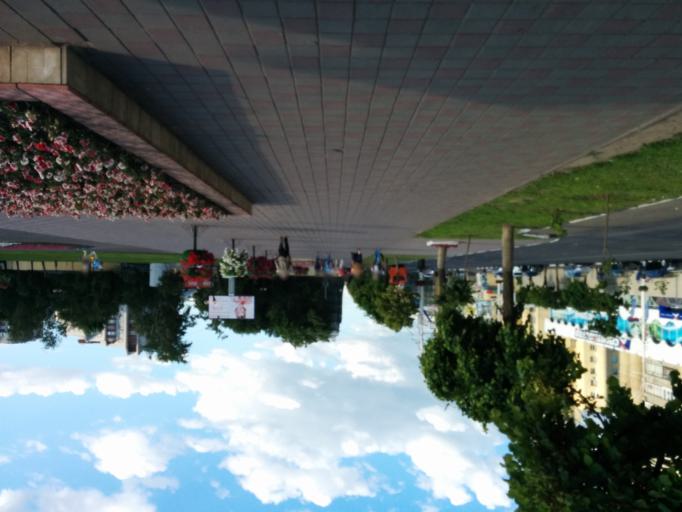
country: RU
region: Tambov
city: Tambov
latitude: 52.7334
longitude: 41.4529
